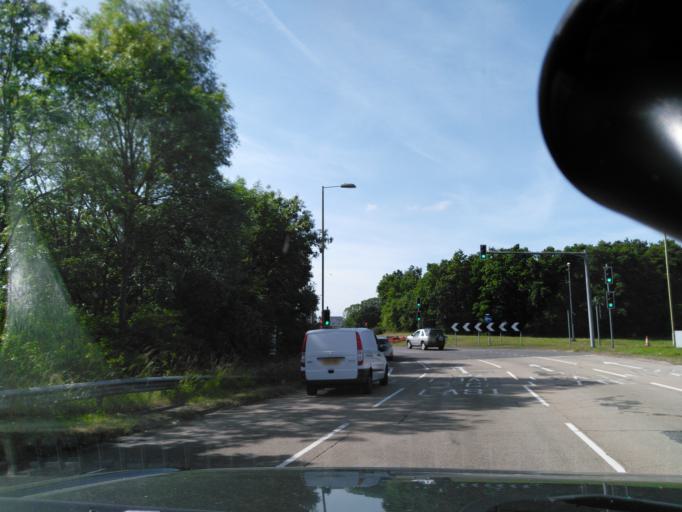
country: GB
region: England
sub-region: Hampshire
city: Botley
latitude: 50.8700
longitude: -1.2543
